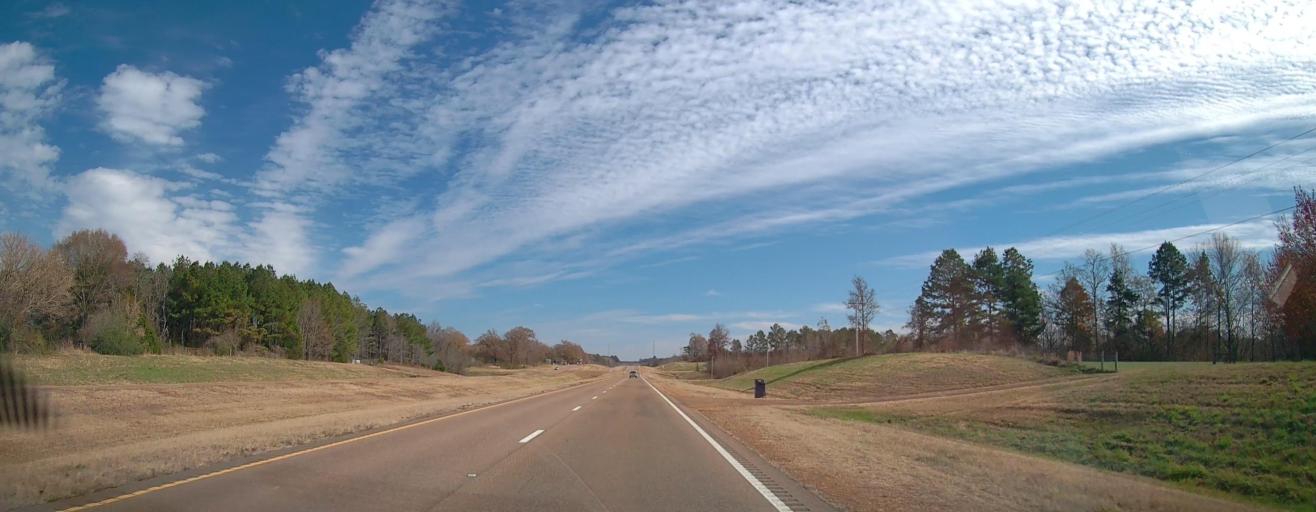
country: US
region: Mississippi
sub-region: Benton County
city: Ashland
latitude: 34.9458
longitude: -89.1761
